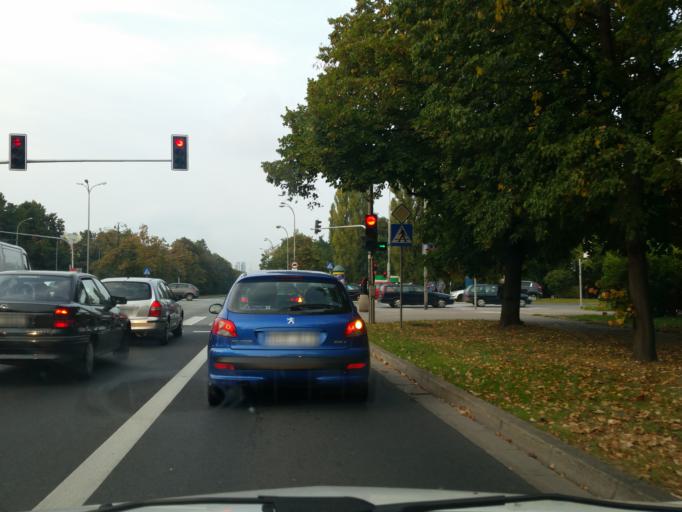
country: PL
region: Masovian Voivodeship
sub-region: Warszawa
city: Ochota
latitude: 52.1980
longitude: 20.9840
